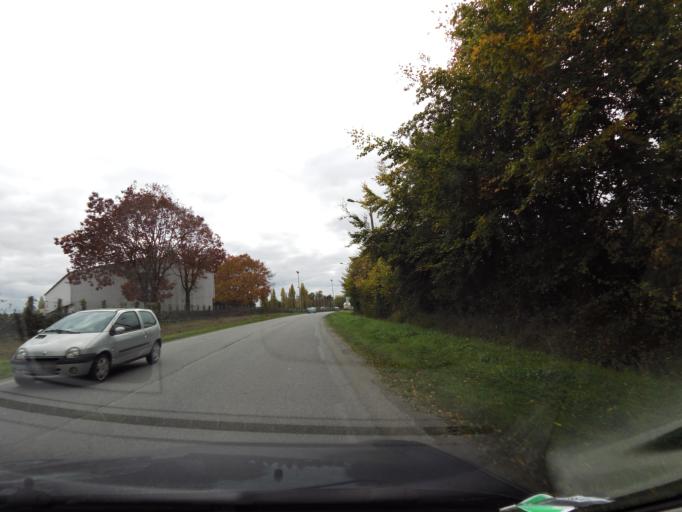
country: FR
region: Brittany
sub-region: Departement d'Ille-et-Vilaine
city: Vern-sur-Seiche
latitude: 48.0514
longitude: -1.6039
